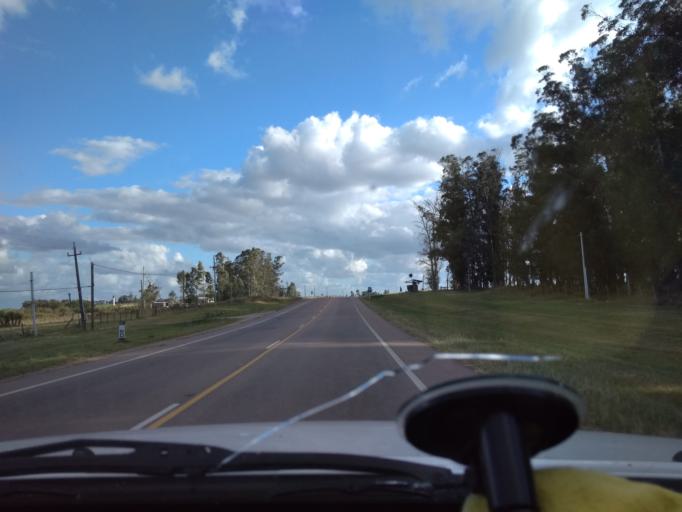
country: UY
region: Canelones
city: San Jacinto
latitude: -34.4961
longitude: -55.8321
